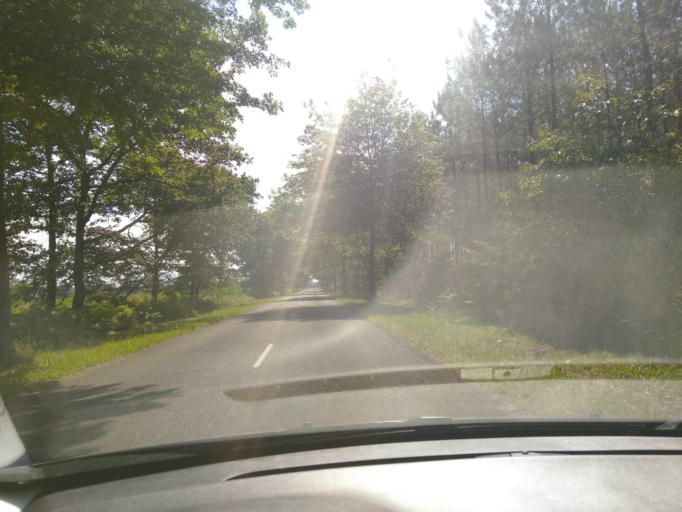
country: FR
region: Aquitaine
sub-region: Departement des Landes
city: Saint-Vincent-de-Paul
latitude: 43.7841
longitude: -0.9822
